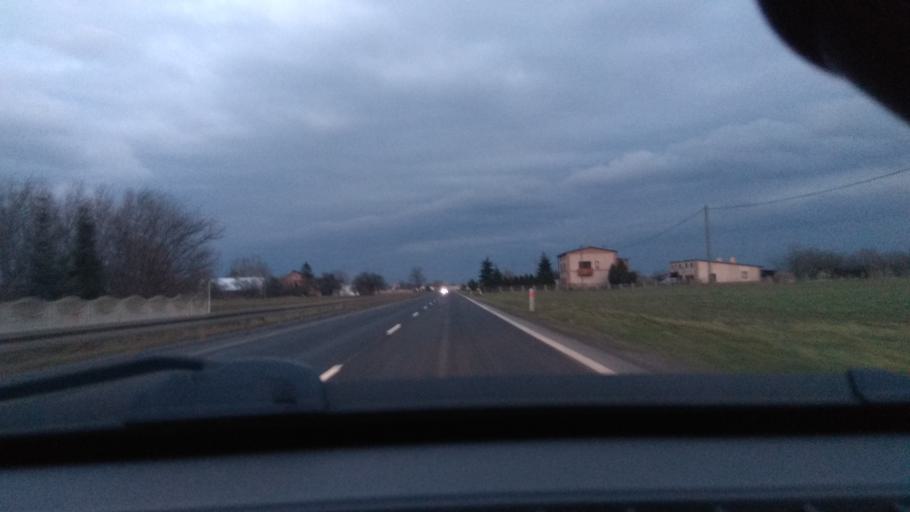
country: PL
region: Greater Poland Voivodeship
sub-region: Powiat kepinski
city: Slupia pod Kepnem
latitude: 51.2978
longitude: 18.0673
